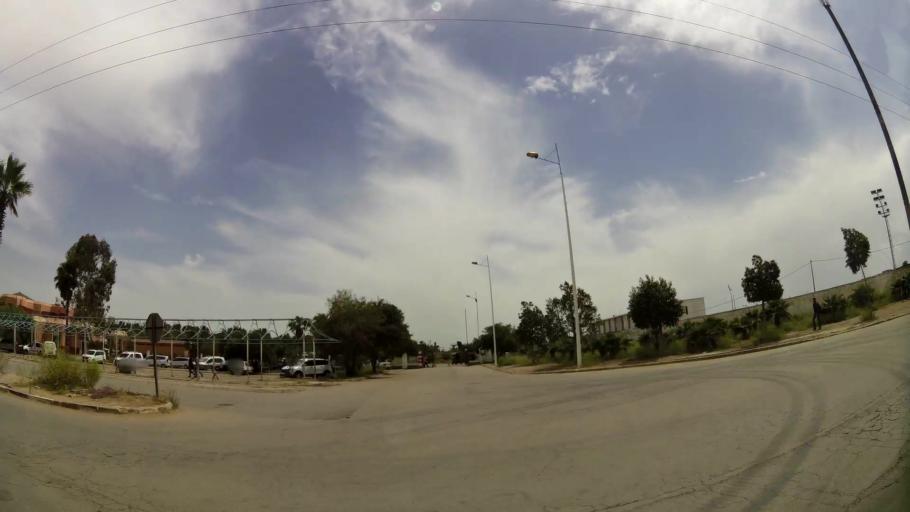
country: MA
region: Rabat-Sale-Zemmour-Zaer
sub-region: Khemisset
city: Khemisset
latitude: 33.8213
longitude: -6.0742
